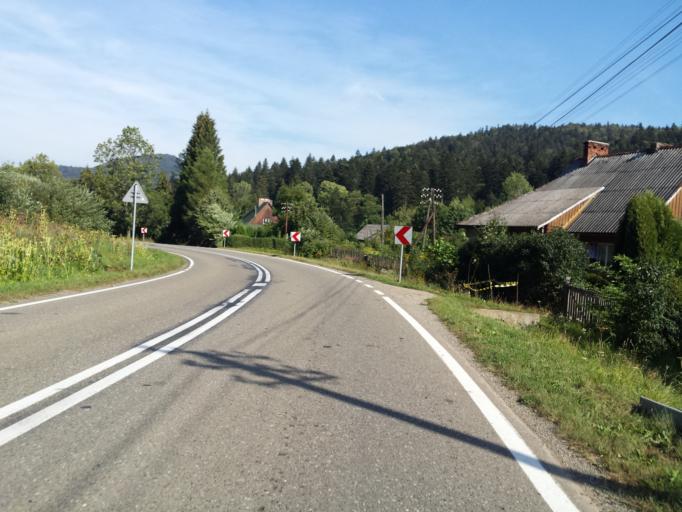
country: PL
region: Subcarpathian Voivodeship
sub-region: Powiat leski
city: Baligrod
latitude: 49.2829
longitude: 22.2788
